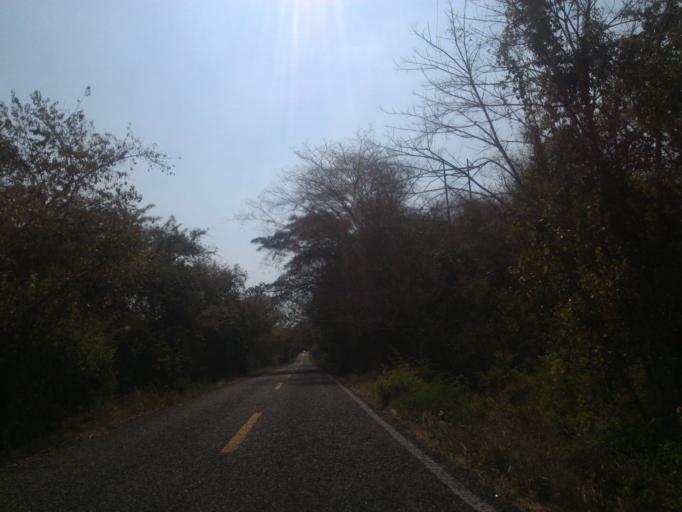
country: MX
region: Michoacan
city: Coahuayana Viejo
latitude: 18.3677
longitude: -103.5069
